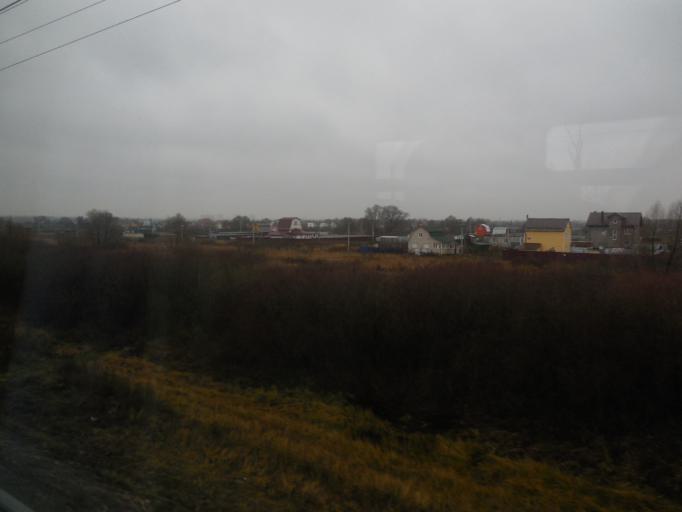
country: RU
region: Moskovskaya
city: Yam
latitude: 55.5073
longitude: 37.7195
